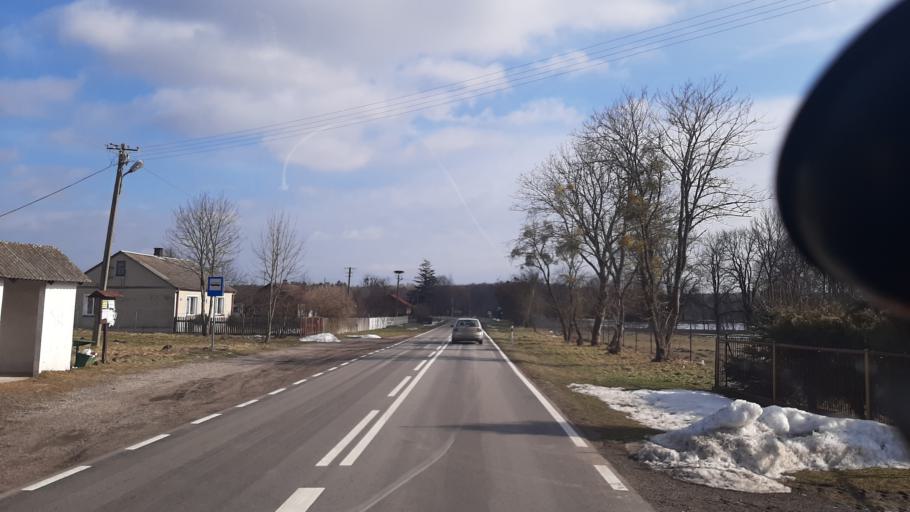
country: PL
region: Lublin Voivodeship
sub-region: Powiat parczewski
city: Sosnowica
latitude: 51.4968
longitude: 23.1707
